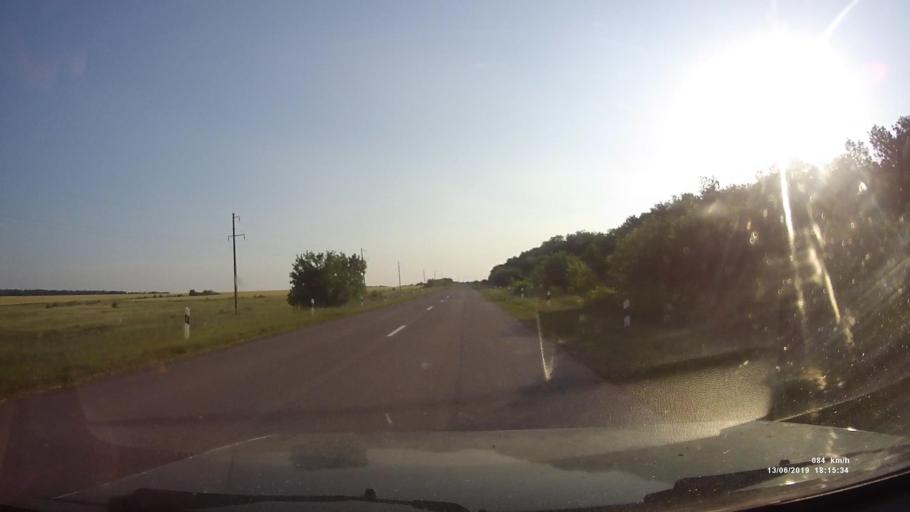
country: RU
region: Rostov
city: Kazanskaya
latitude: 49.9309
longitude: 41.3548
